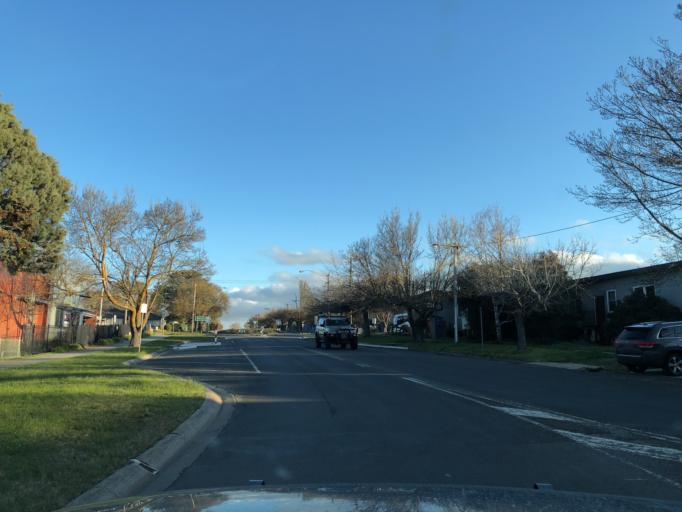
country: AU
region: Victoria
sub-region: Moorabool
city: Bacchus Marsh
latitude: -37.5992
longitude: 144.2282
